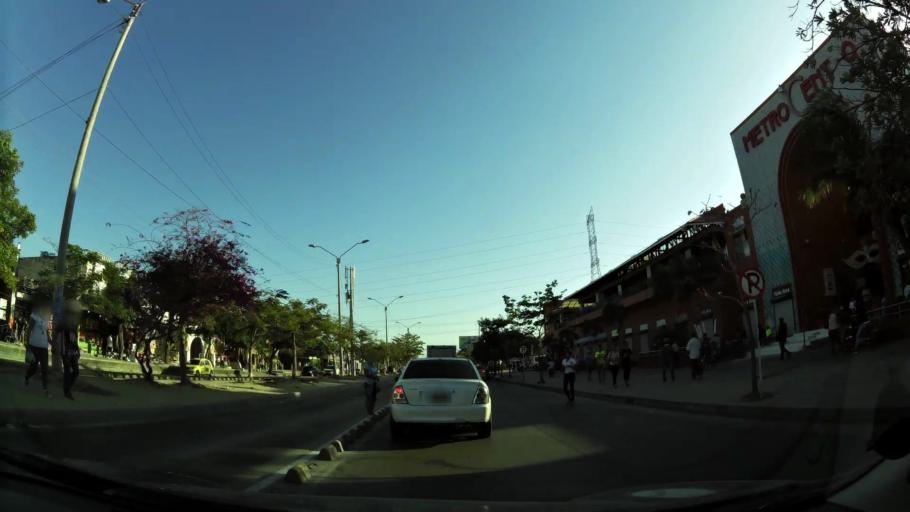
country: CO
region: Atlantico
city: Soledad
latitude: 10.9312
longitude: -74.7993
